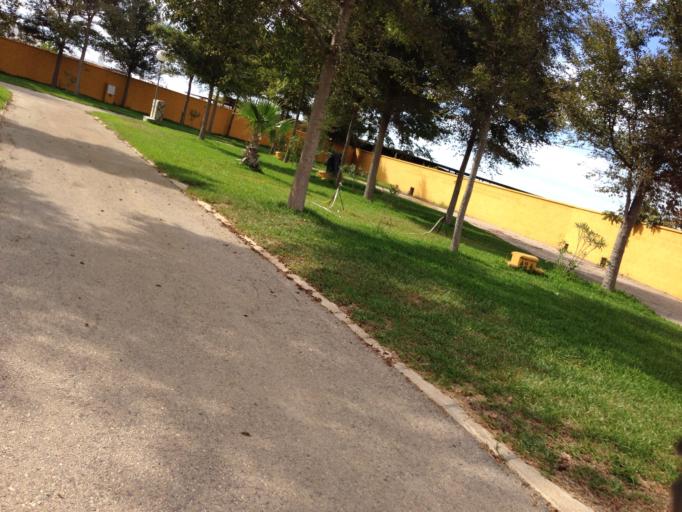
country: ES
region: Andalusia
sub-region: Provincia de Cadiz
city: Conil de la Frontera
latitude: 36.3137
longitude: -6.1139
